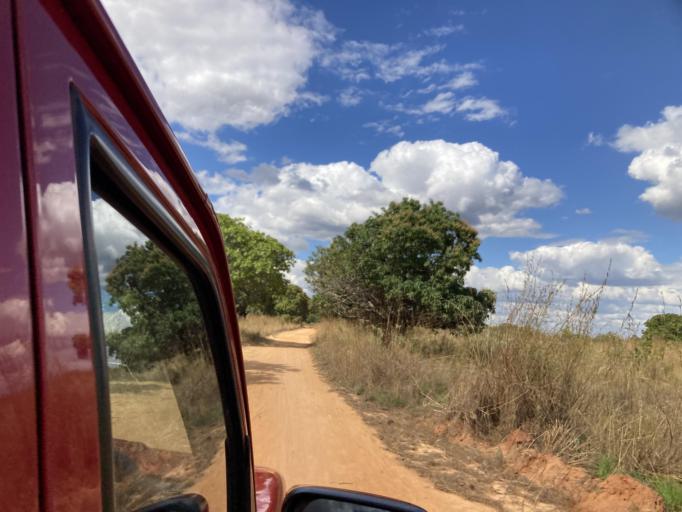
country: MZ
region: Cabo Delgado
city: Montepuez
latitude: -13.1259
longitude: 39.0440
